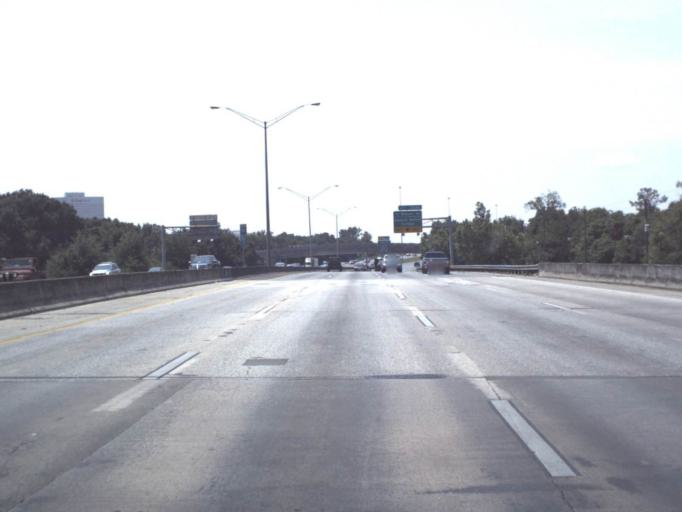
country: US
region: Florida
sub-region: Duval County
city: Jacksonville
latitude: 30.3432
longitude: -81.6683
